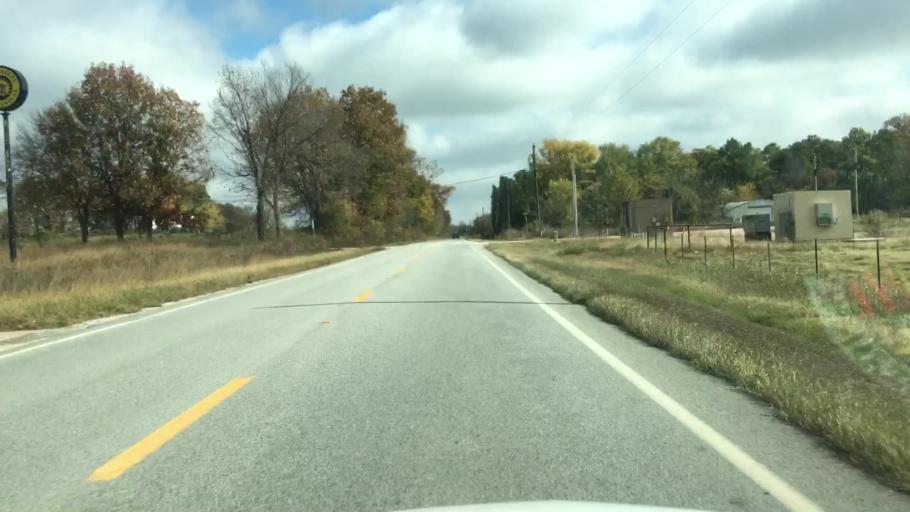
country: US
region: Arkansas
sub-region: Benton County
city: Gentry
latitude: 36.2576
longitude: -94.3962
